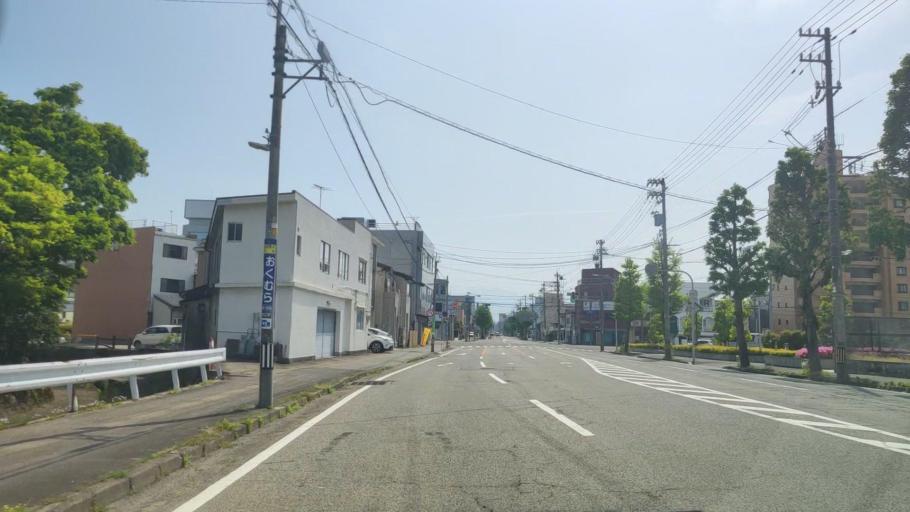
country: JP
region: Toyama
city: Toyama-shi
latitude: 36.6970
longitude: 137.2196
